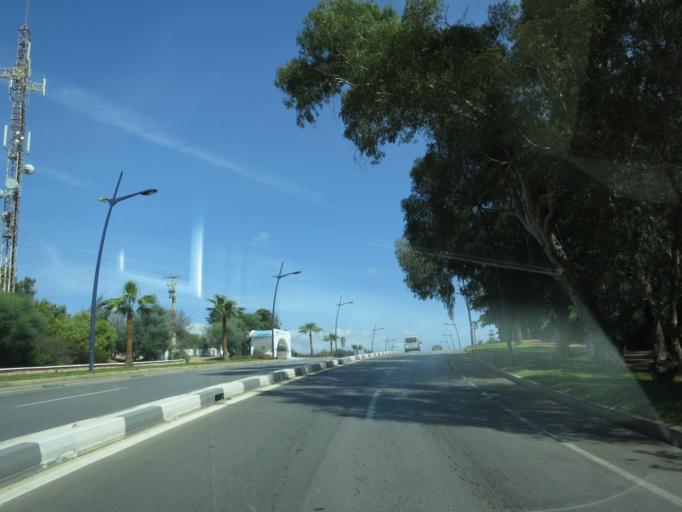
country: ES
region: Ceuta
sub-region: Ceuta
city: Ceuta
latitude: 35.7754
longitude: -5.3488
